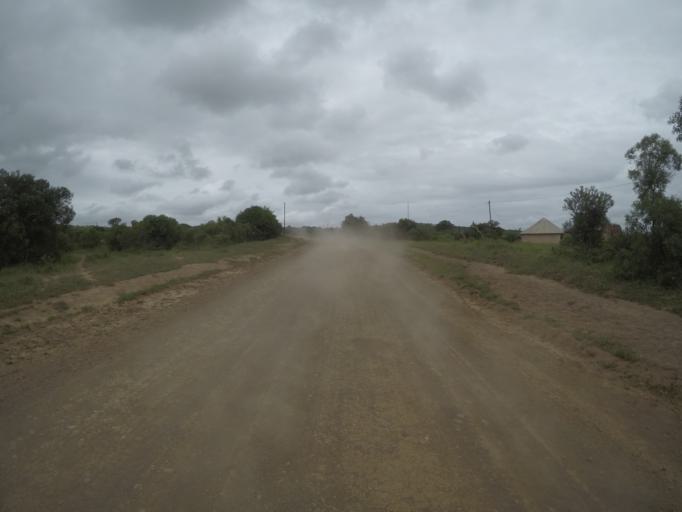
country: ZA
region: KwaZulu-Natal
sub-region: uThungulu District Municipality
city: Empangeni
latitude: -28.5978
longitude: 31.8381
